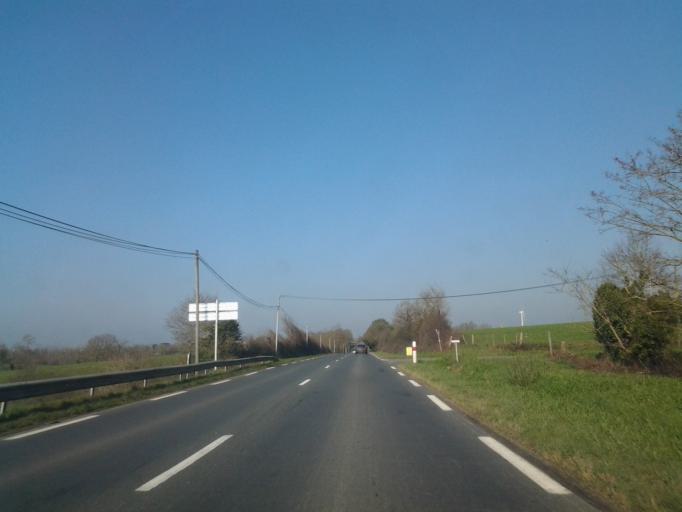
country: FR
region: Pays de la Loire
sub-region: Departement de la Vendee
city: Mache
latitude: 46.7748
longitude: -1.6753
